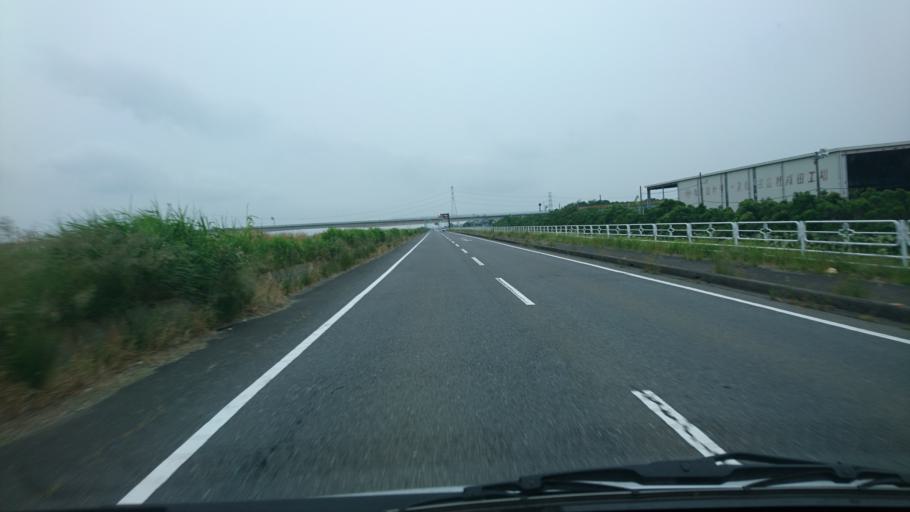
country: JP
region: Ibaraki
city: Inashiki
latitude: 35.8986
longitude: 140.3721
